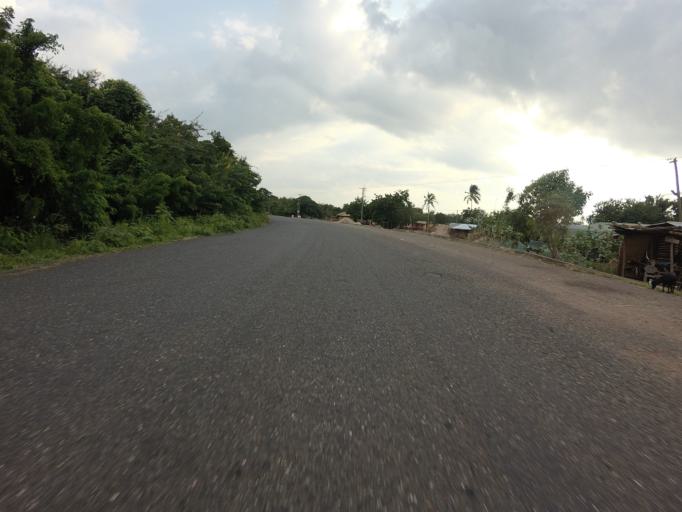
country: GH
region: Volta
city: Ho
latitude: 6.5054
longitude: 0.4899
